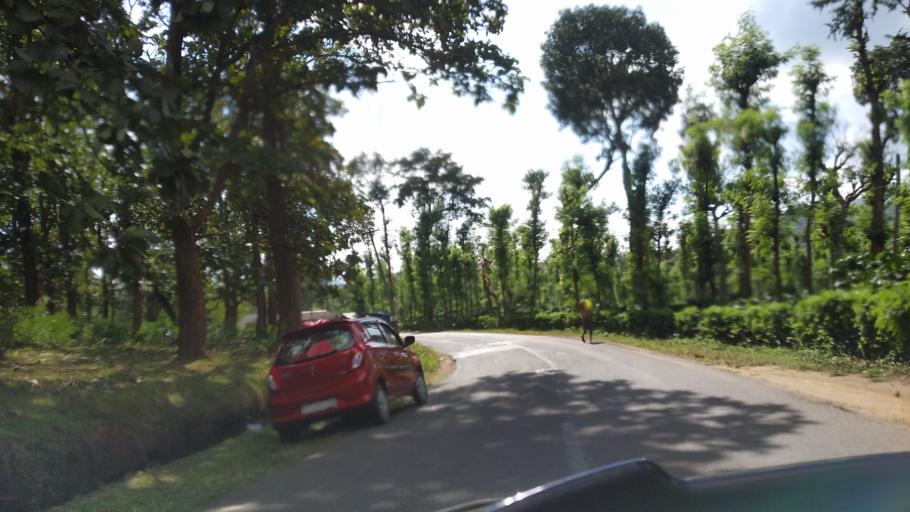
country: IN
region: Kerala
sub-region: Wayanad
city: Panamaram
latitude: 11.9421
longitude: 76.0643
